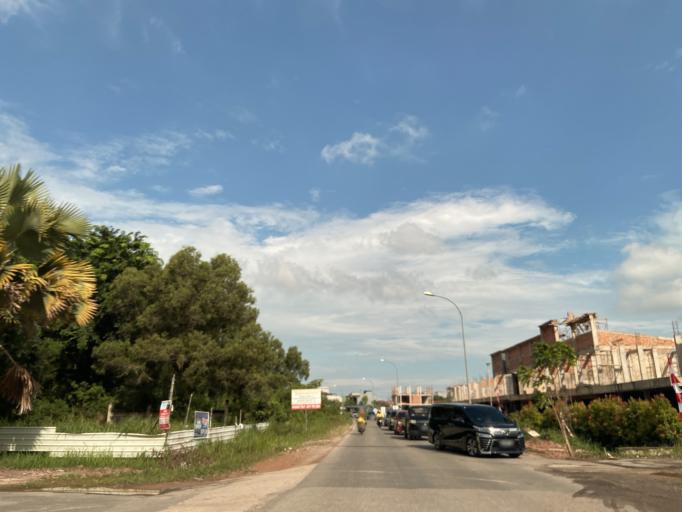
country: SG
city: Singapore
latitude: 1.1133
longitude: 104.0301
